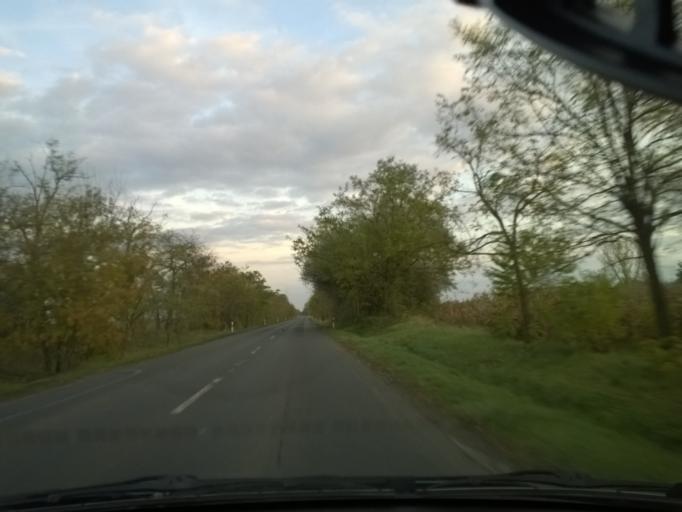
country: HU
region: Bacs-Kiskun
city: Palmonostora
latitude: 46.6950
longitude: 19.9322
